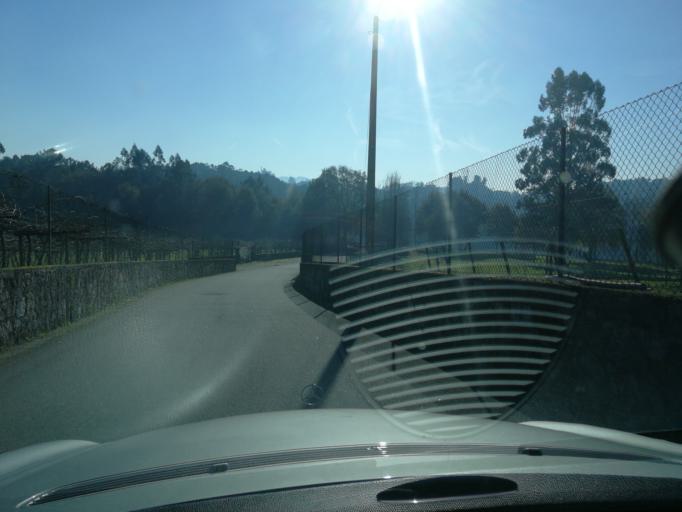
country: PT
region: Braga
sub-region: Braga
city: Adaufe
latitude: 41.6091
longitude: -8.4002
